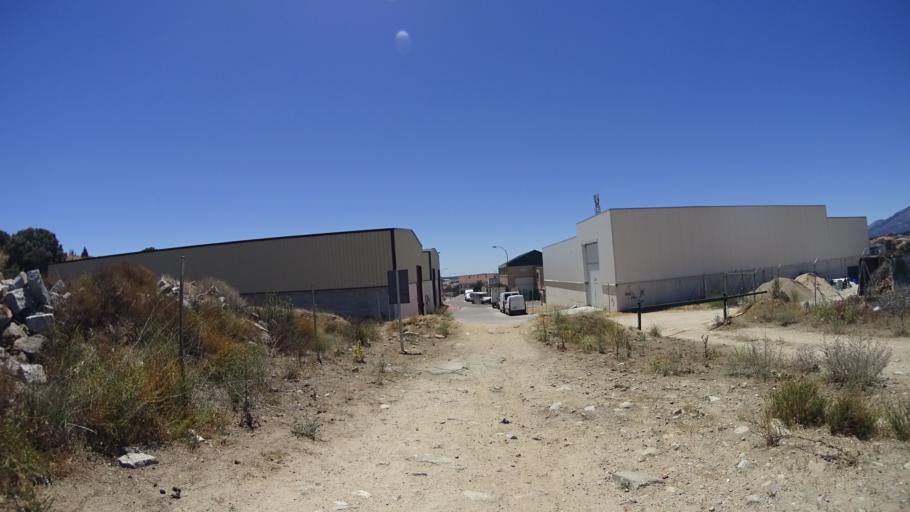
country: ES
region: Madrid
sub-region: Provincia de Madrid
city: Alpedrete
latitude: 40.6628
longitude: -4.0190
